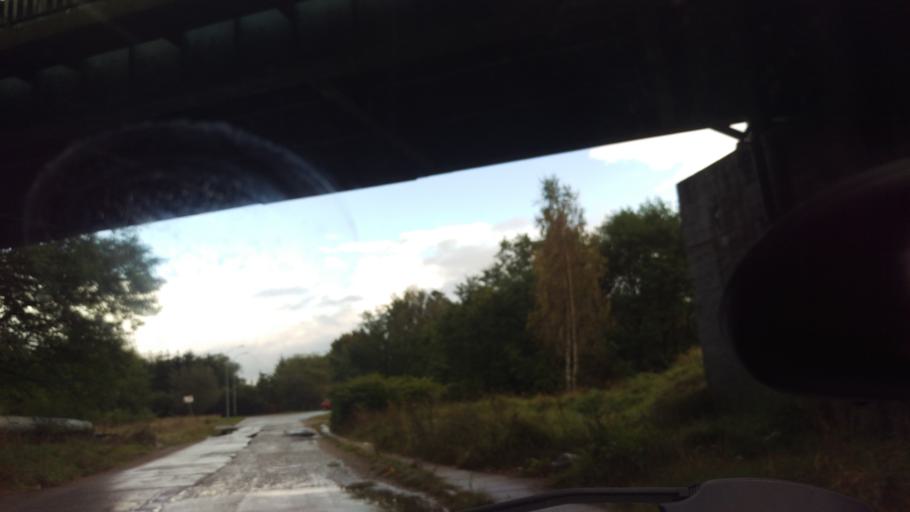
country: PL
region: West Pomeranian Voivodeship
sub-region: Powiat gryfinski
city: Stare Czarnowo
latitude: 53.3735
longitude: 14.6811
